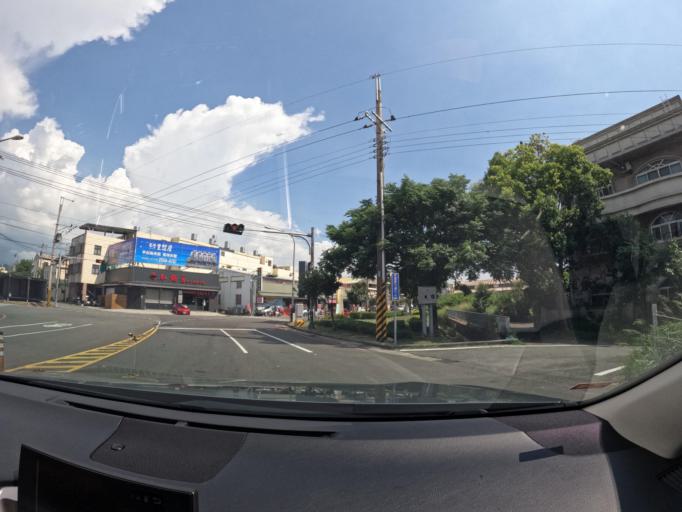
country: TW
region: Taiwan
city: Fengyuan
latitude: 24.3119
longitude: 120.7183
